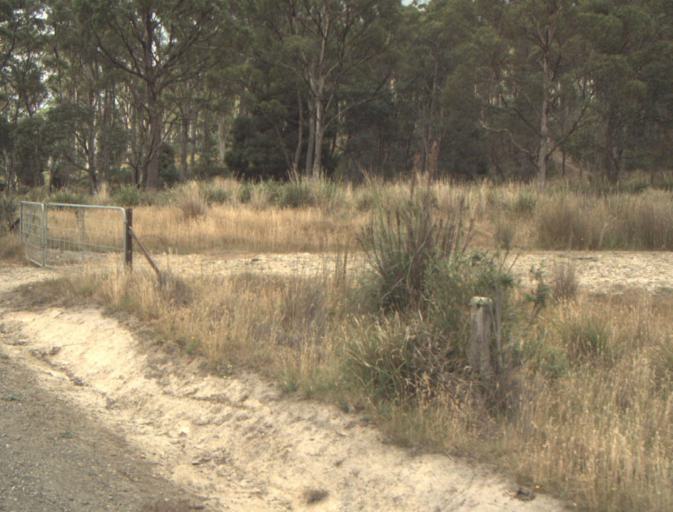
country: AU
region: Tasmania
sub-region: Northern Midlands
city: Evandale
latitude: -41.4635
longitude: 147.4490
